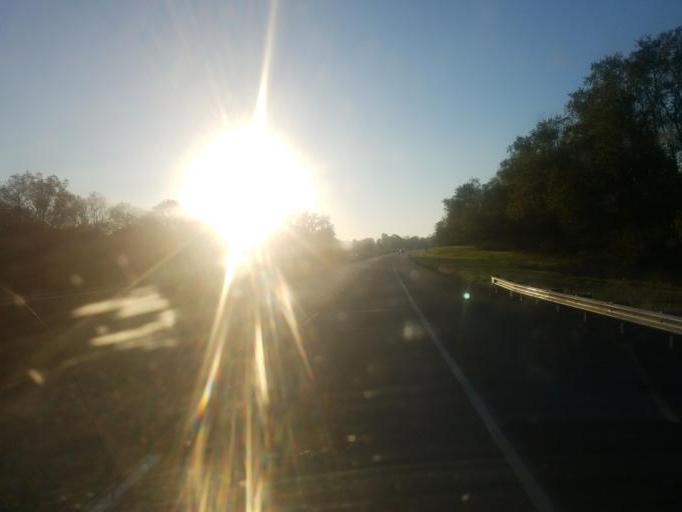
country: US
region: Pennsylvania
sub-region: Butler County
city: Fernway
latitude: 40.7348
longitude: -80.1702
